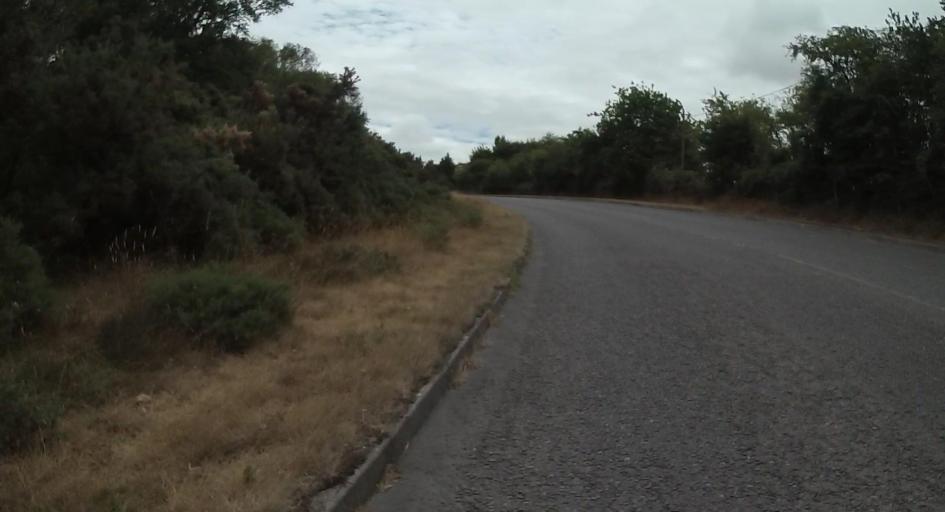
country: GB
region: England
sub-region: Dorset
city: Wareham
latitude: 50.6664
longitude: -2.1033
